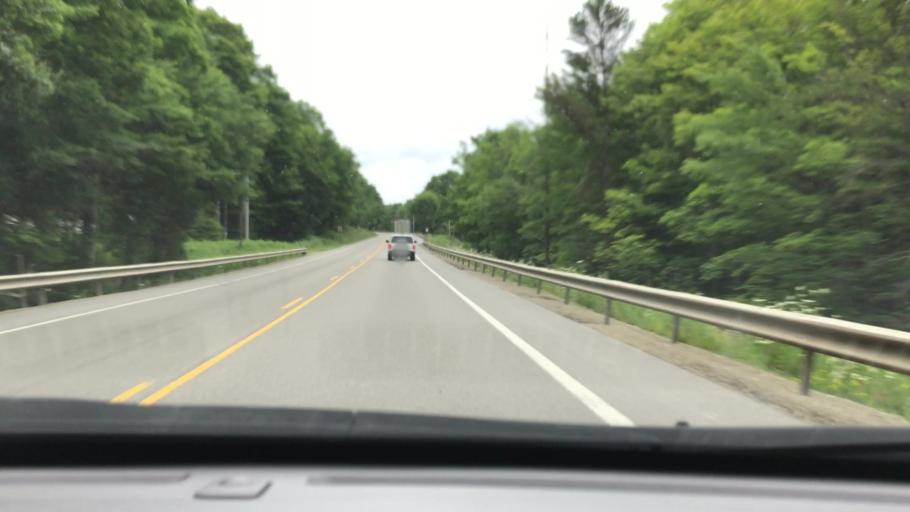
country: US
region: Pennsylvania
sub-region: McKean County
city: Kane
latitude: 41.6970
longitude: -78.6912
